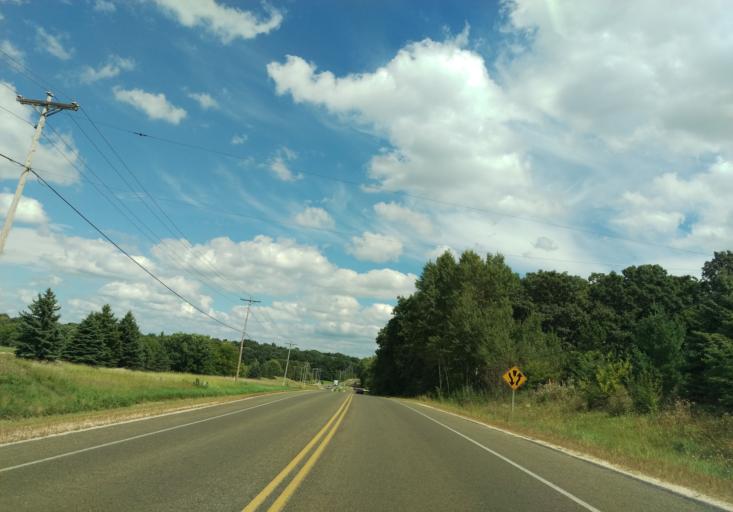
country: US
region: Wisconsin
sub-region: Dane County
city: Shorewood Hills
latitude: 43.1130
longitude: -89.4578
